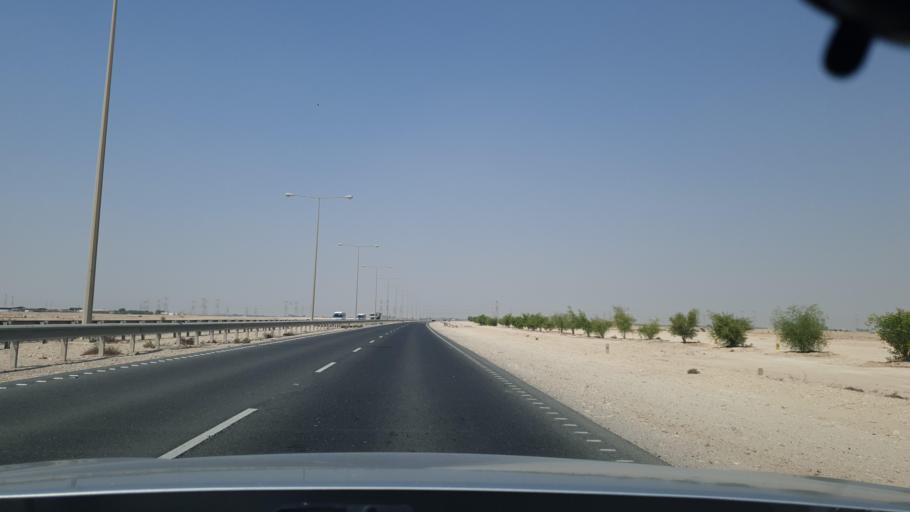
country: QA
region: Al Khawr
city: Al Khawr
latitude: 25.7408
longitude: 51.4867
